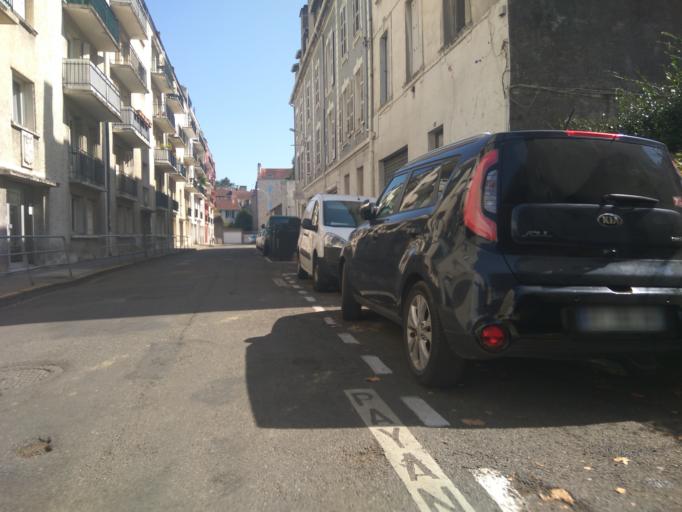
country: FR
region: Aquitaine
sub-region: Departement des Pyrenees-Atlantiques
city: Pau
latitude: 43.3003
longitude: -0.3749
